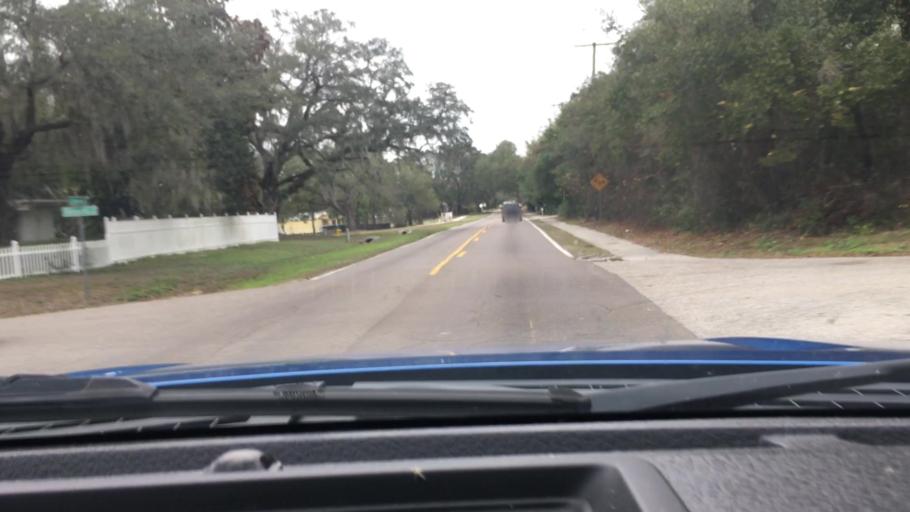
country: US
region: Florida
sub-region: Hillsborough County
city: Mango
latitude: 27.9628
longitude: -82.3104
